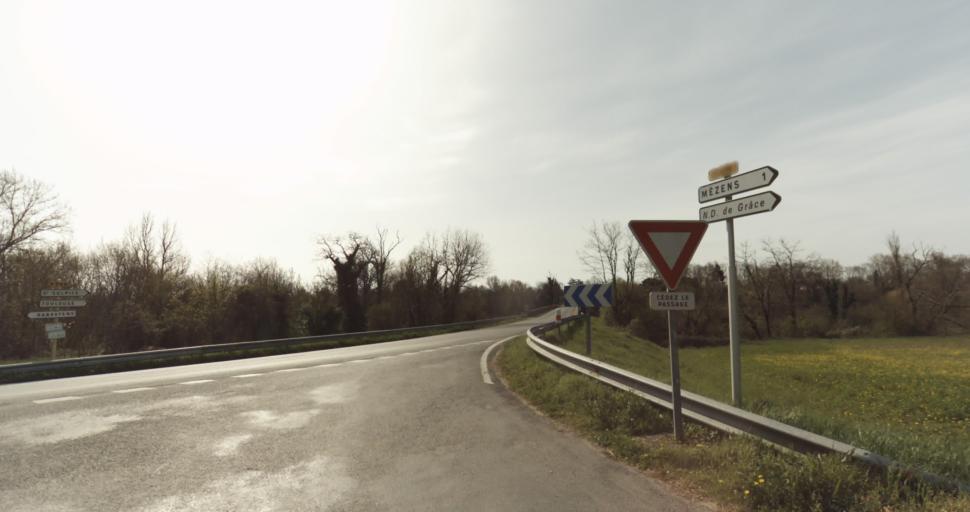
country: FR
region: Midi-Pyrenees
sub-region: Departement du Tarn
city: Saint-Sulpice-la-Pointe
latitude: 43.7860
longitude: 1.6783
